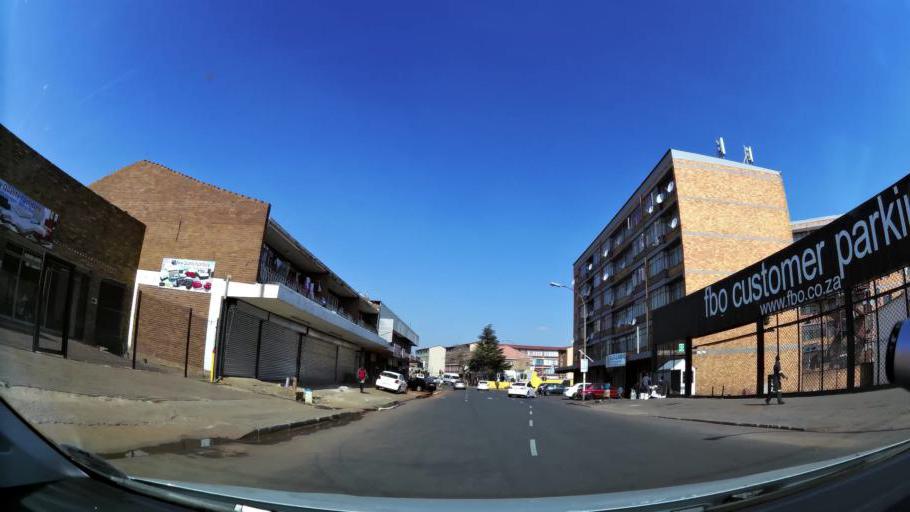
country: ZA
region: Gauteng
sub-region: City of Johannesburg Metropolitan Municipality
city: Modderfontein
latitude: -26.1106
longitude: 28.2308
